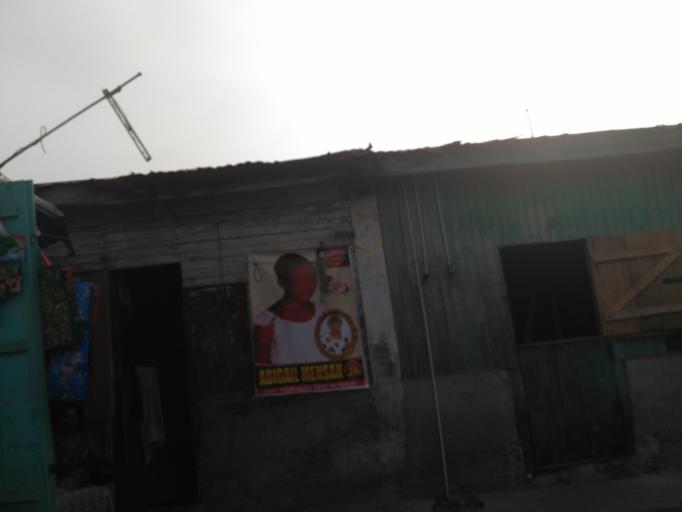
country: GH
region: Ashanti
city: Kumasi
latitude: 6.6777
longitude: -1.5911
